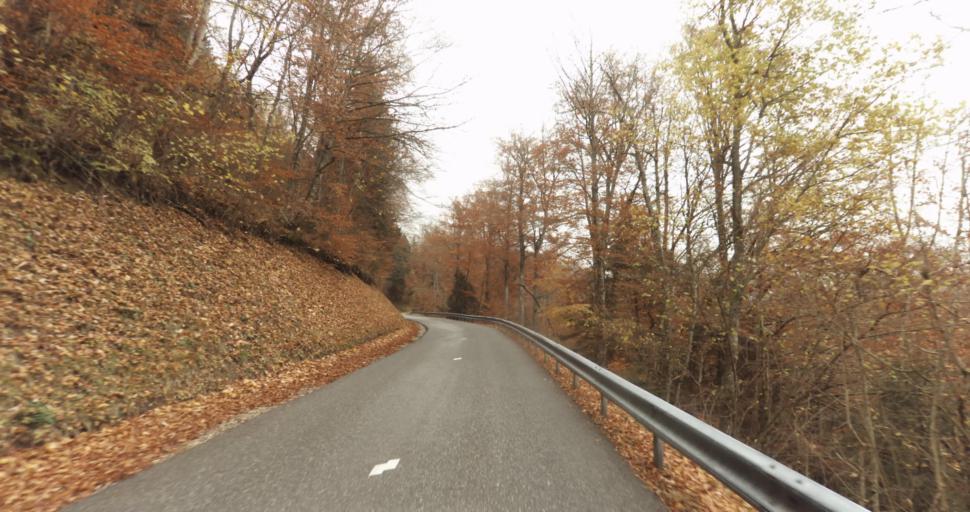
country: FR
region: Rhone-Alpes
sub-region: Departement de la Haute-Savoie
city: Thorens-Glieres
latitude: 45.9732
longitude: 6.2926
